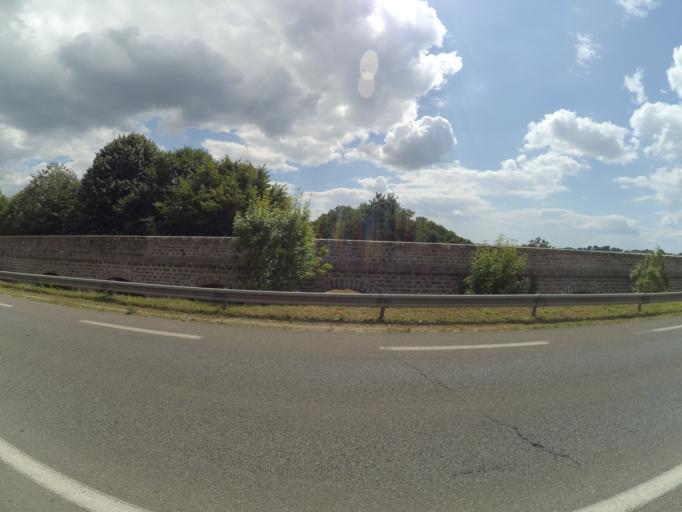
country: FR
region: Brittany
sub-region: Departement du Morbihan
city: Lanester
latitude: 47.7643
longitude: -3.3001
